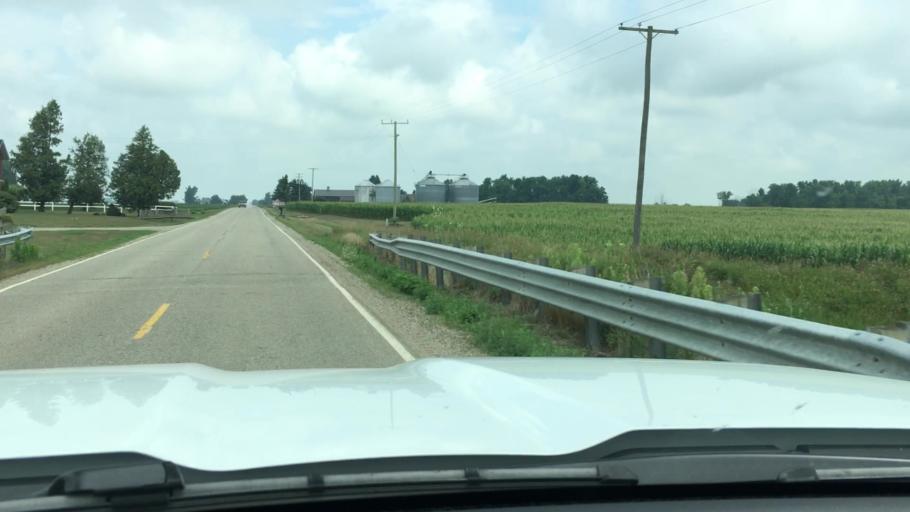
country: US
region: Michigan
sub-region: Sanilac County
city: Marlette
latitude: 43.3646
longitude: -83.0059
